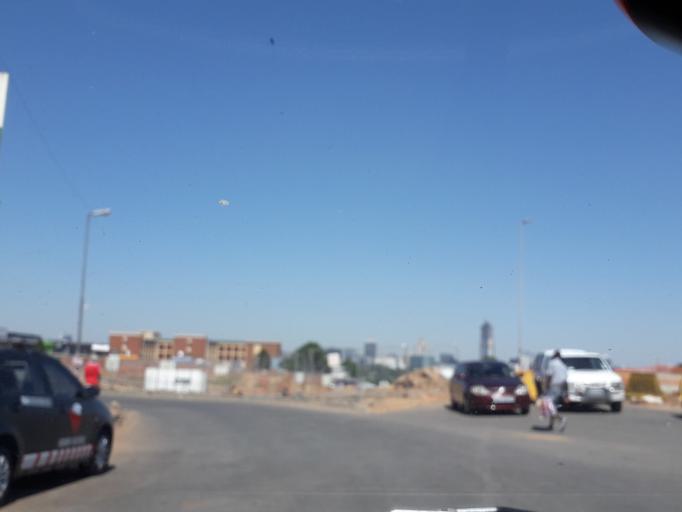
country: ZA
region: Gauteng
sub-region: City of Johannesburg Metropolitan Municipality
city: Modderfontein
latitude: -26.1102
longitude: 28.0857
